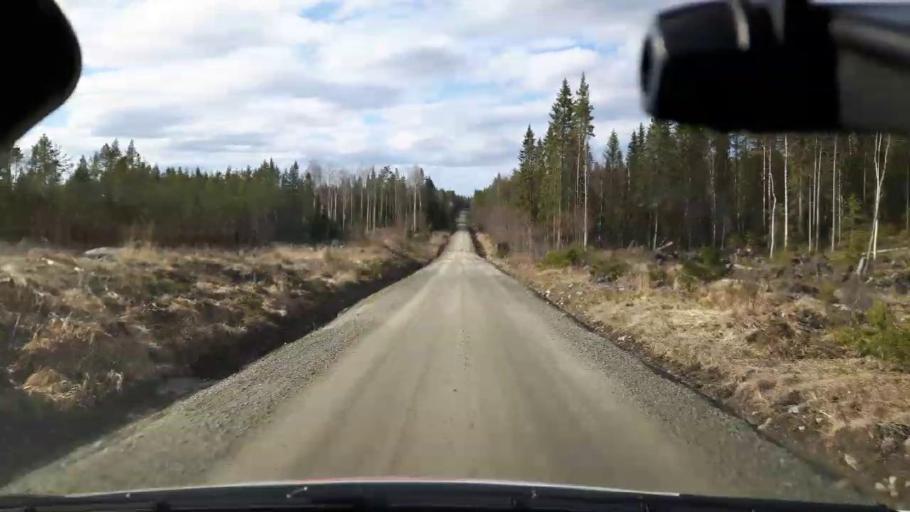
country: SE
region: Jaemtland
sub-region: Bergs Kommun
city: Hoverberg
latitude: 62.8596
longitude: 14.6671
